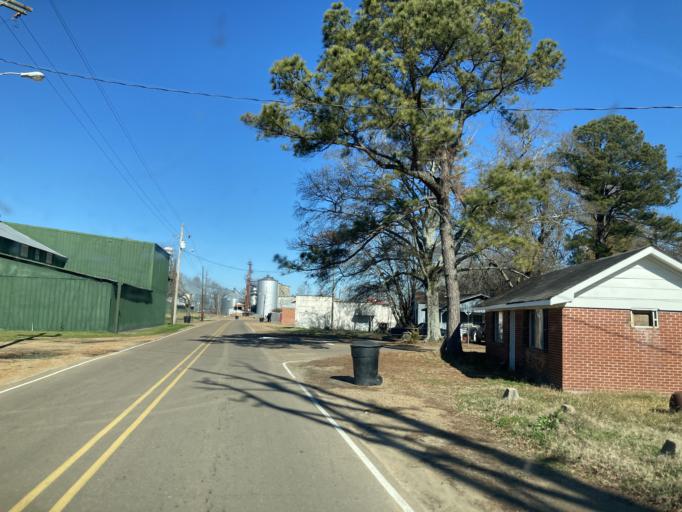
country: US
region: Mississippi
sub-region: Yazoo County
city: Yazoo City
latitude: 32.9796
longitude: -90.5917
